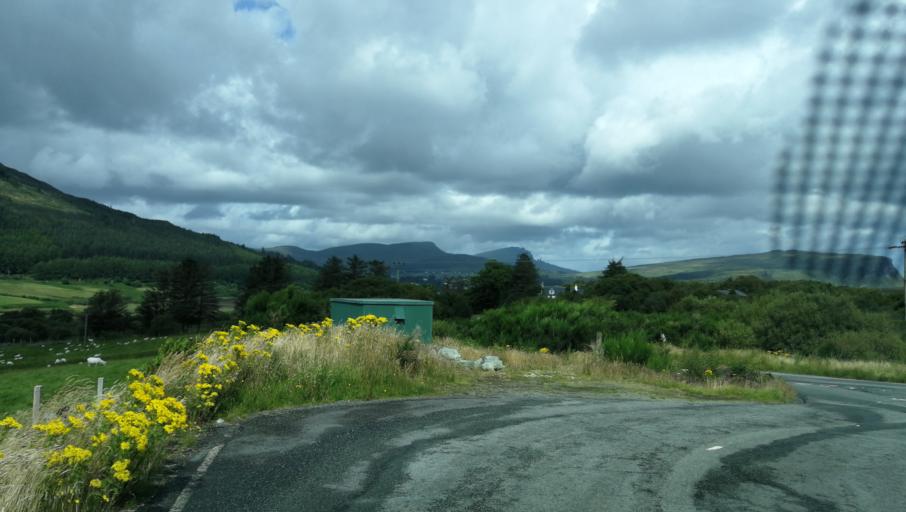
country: GB
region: Scotland
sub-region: Highland
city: Portree
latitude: 57.3857
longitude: -6.1951
